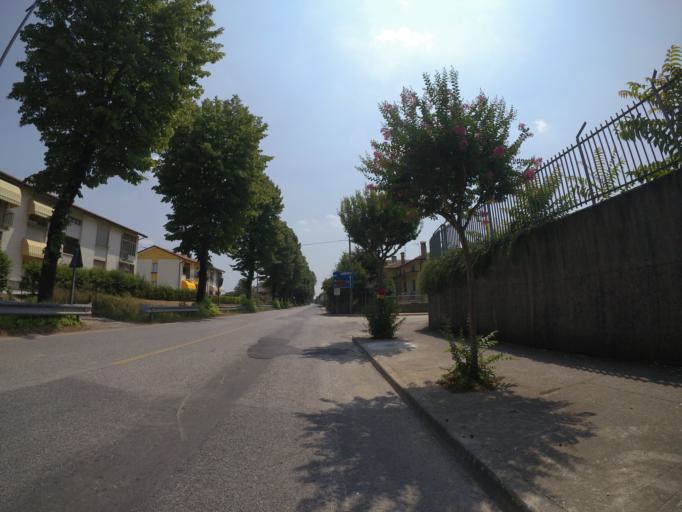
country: IT
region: Friuli Venezia Giulia
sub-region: Provincia di Udine
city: Basiliano-Vissandone
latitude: 46.0119
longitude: 13.1110
